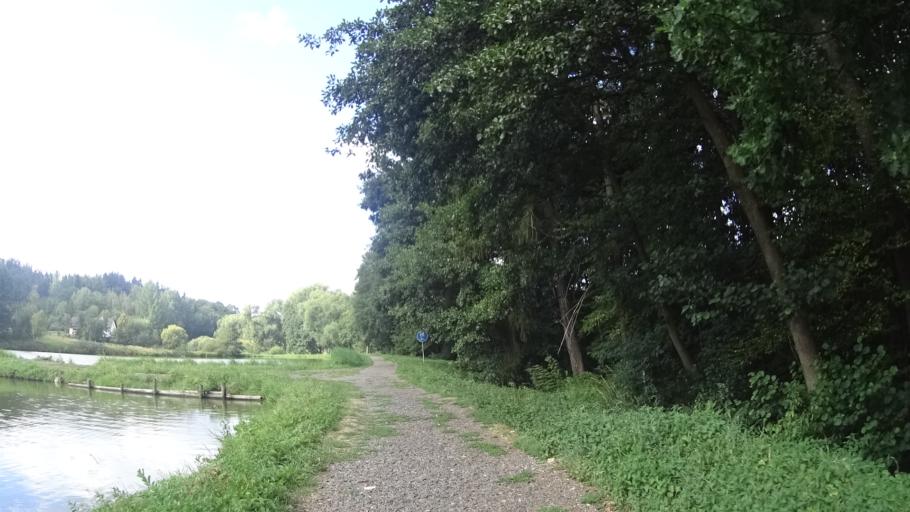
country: CZ
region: Pardubicky
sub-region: Okres Usti nad Orlici
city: Lanskroun
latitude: 49.9227
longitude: 16.5670
